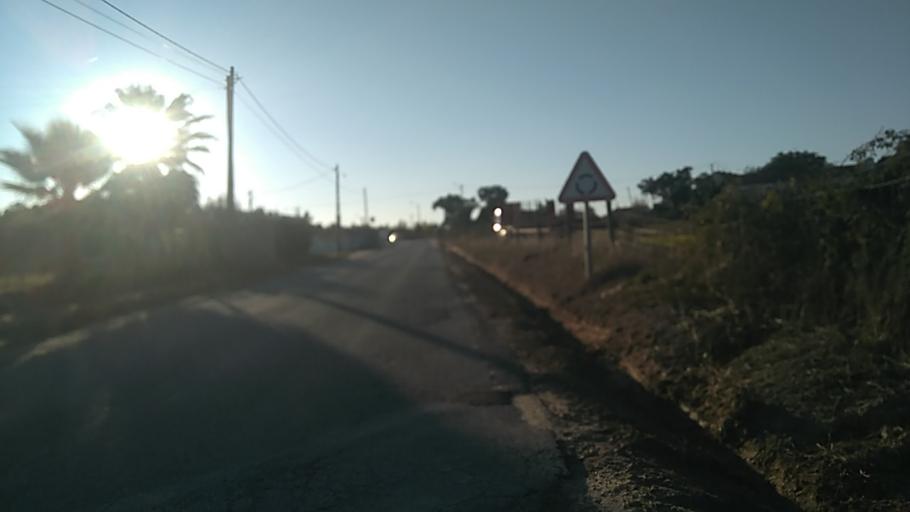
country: PT
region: Evora
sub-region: Vendas Novas
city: Vendas Novas
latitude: 38.8057
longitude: -8.4109
